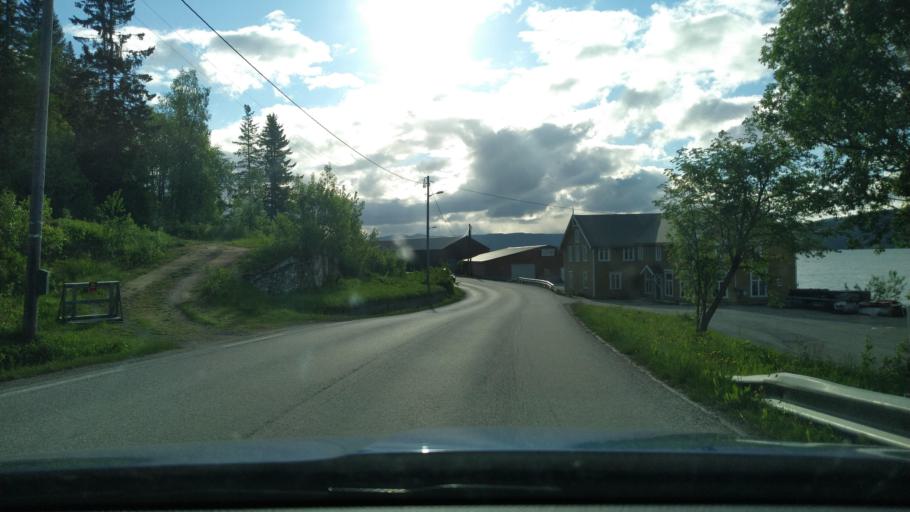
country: NO
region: Troms
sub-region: Sorreisa
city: Sorreisa
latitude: 69.1445
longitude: 18.1353
